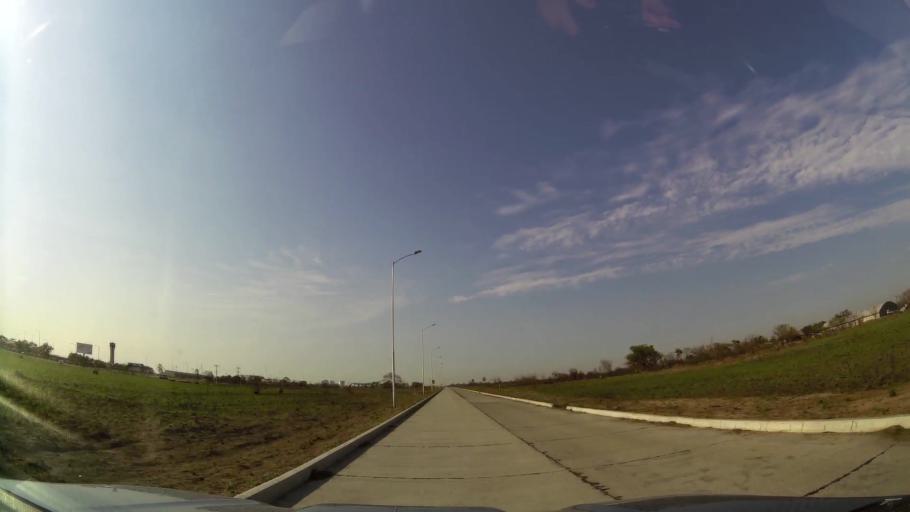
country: BO
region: Santa Cruz
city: La Belgica
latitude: -17.6504
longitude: -63.1424
